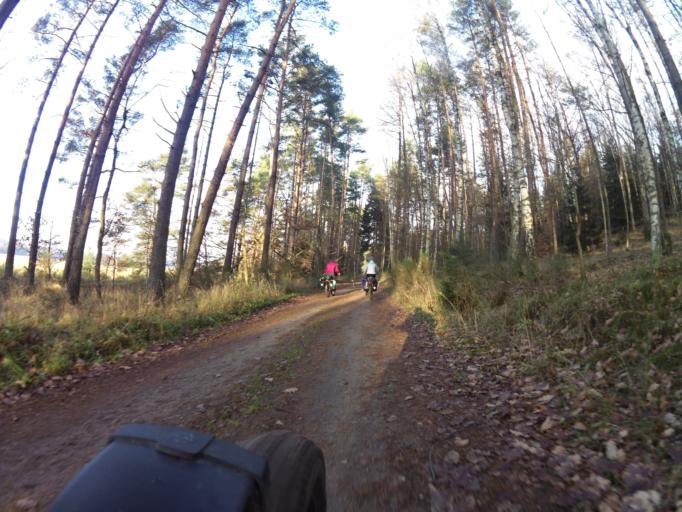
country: PL
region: West Pomeranian Voivodeship
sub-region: Powiat koszalinski
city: Polanow
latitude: 54.0950
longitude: 16.6478
